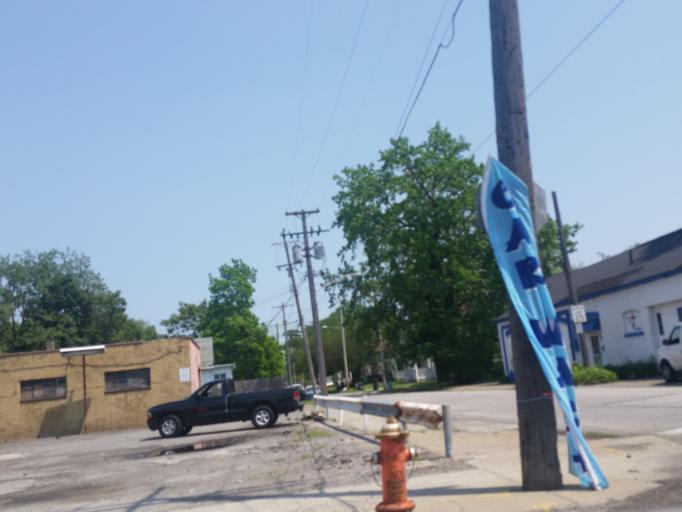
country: US
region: Ohio
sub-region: Cuyahoga County
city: Newburgh Heights
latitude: 41.4905
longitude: -81.6335
